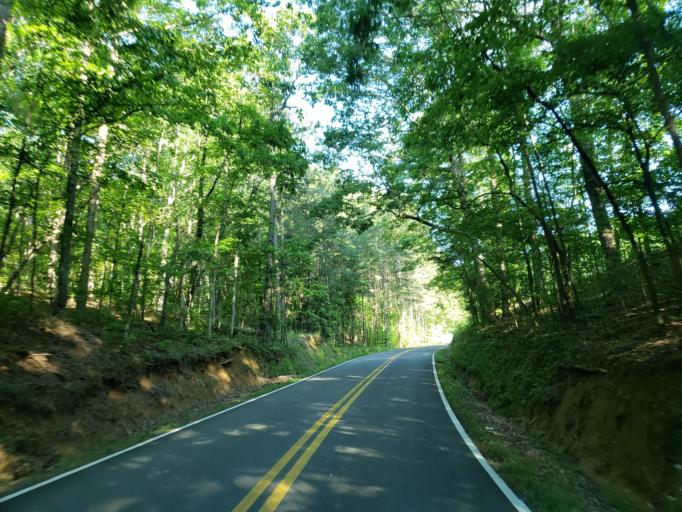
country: US
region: Georgia
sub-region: Murray County
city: Chatsworth
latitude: 34.6625
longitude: -84.6439
